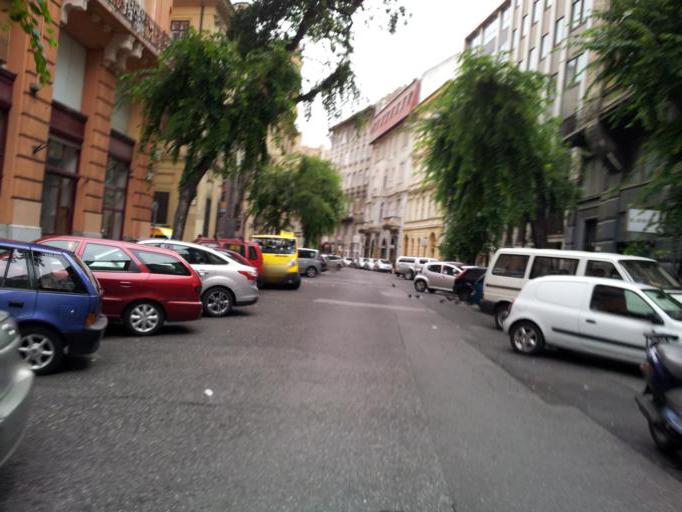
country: HU
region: Budapest
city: Budapest VI. keruelet
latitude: 47.4946
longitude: 19.0586
